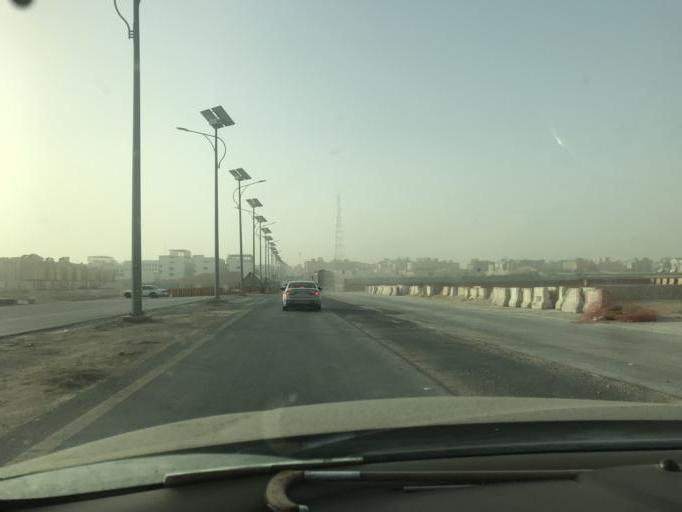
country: SA
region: Ar Riyad
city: Riyadh
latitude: 24.8460
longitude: 46.6640
